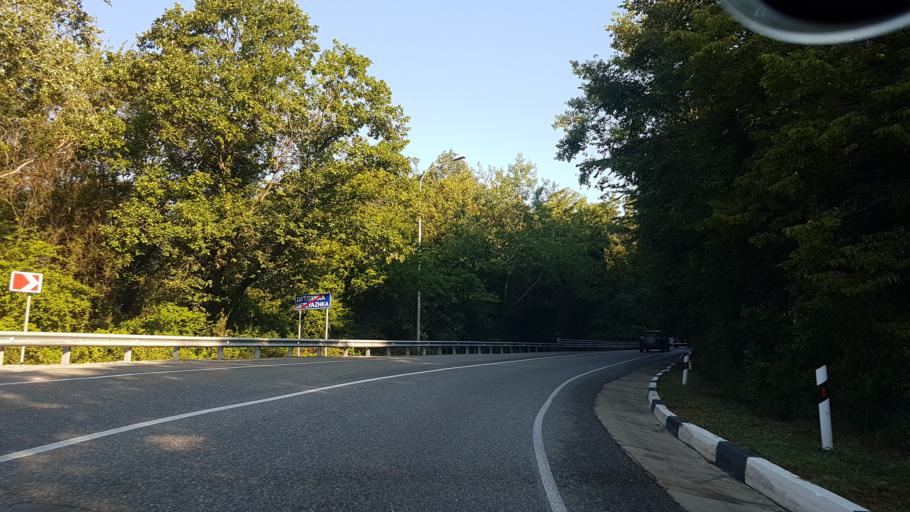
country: RU
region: Krasnodarskiy
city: Vardane
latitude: 43.7525
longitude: 39.5279
